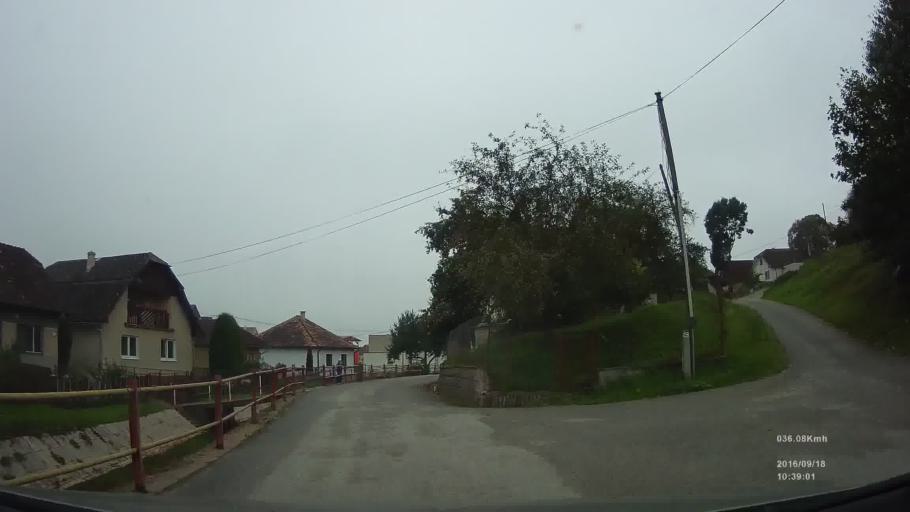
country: SK
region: Kosicky
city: Spisska Nova Ves
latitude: 48.9504
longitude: 20.6201
